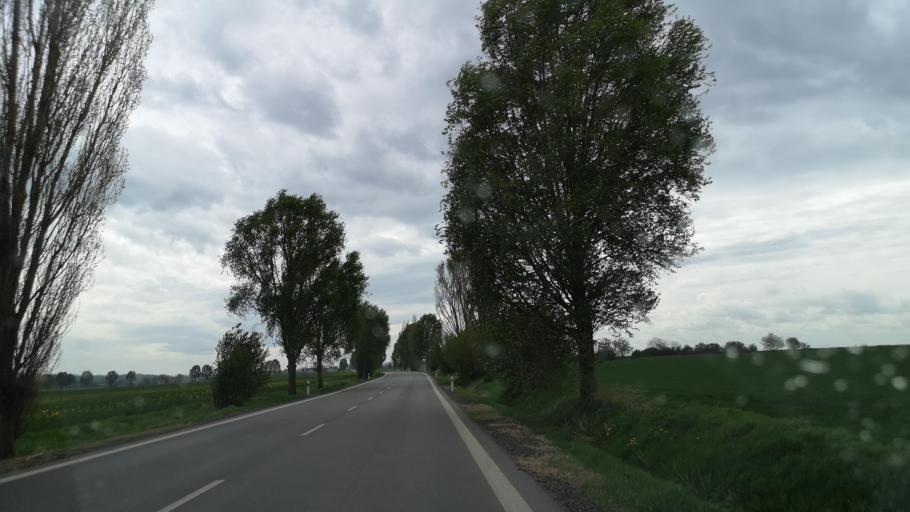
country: SK
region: Nitriansky
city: Zlate Moravce
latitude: 48.3242
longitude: 18.3470
